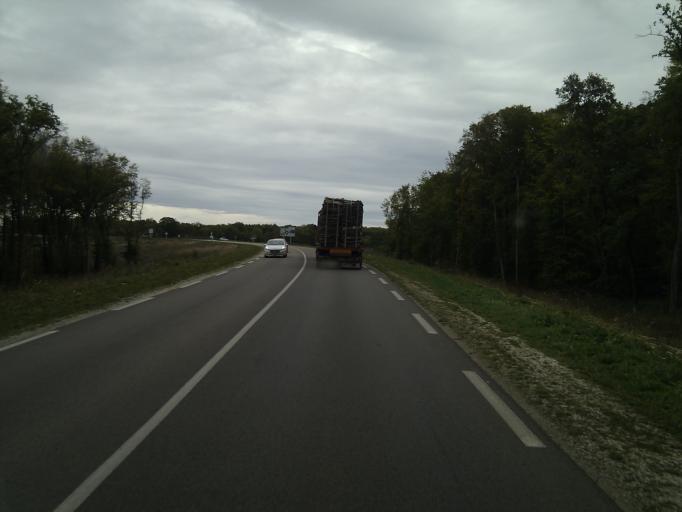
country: FR
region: Champagne-Ardenne
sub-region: Departement de la Haute-Marne
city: Chaumont
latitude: 48.1101
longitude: 5.1051
